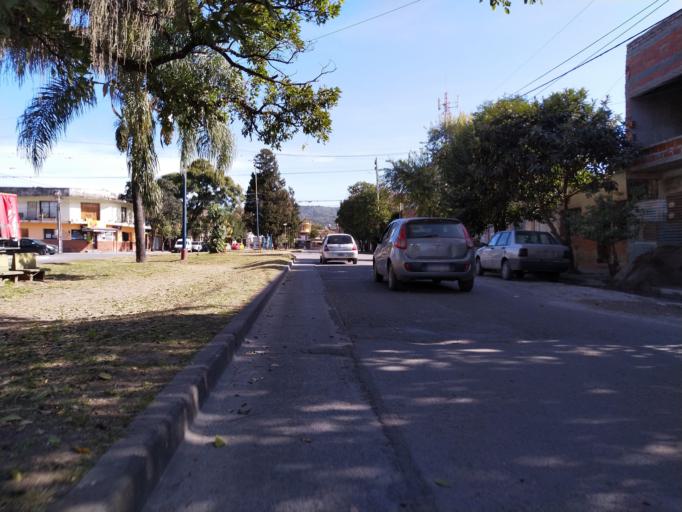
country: AR
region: Jujuy
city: San Salvador de Jujuy
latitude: -24.2009
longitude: -65.2832
